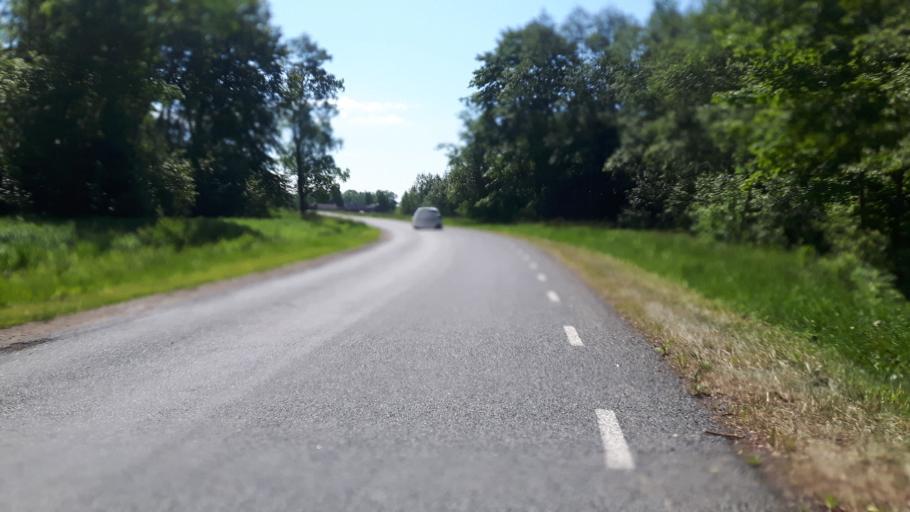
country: EE
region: Paernumaa
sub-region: Vaendra vald (alev)
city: Vandra
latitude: 58.5986
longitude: 25.0218
